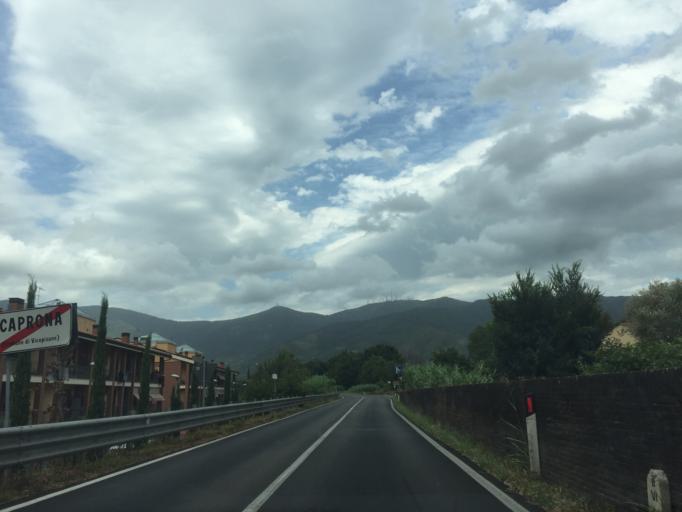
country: IT
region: Tuscany
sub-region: Province of Pisa
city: Gabella
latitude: 43.7086
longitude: 10.5047
